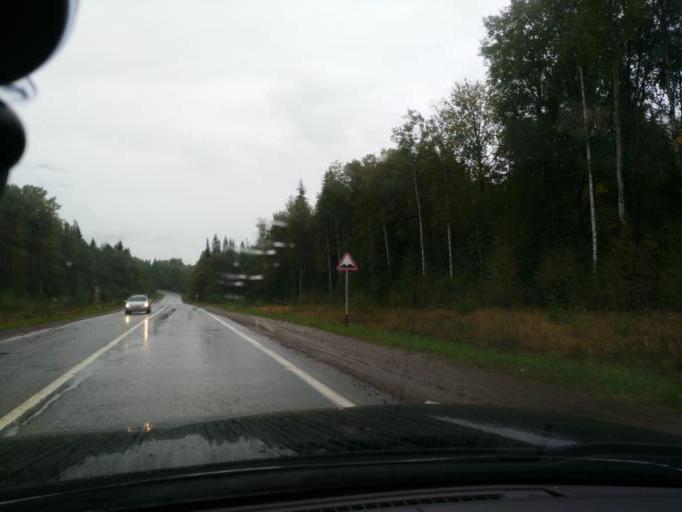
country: RU
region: Perm
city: Yugo-Kamskiy
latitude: 57.5008
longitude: 55.6882
